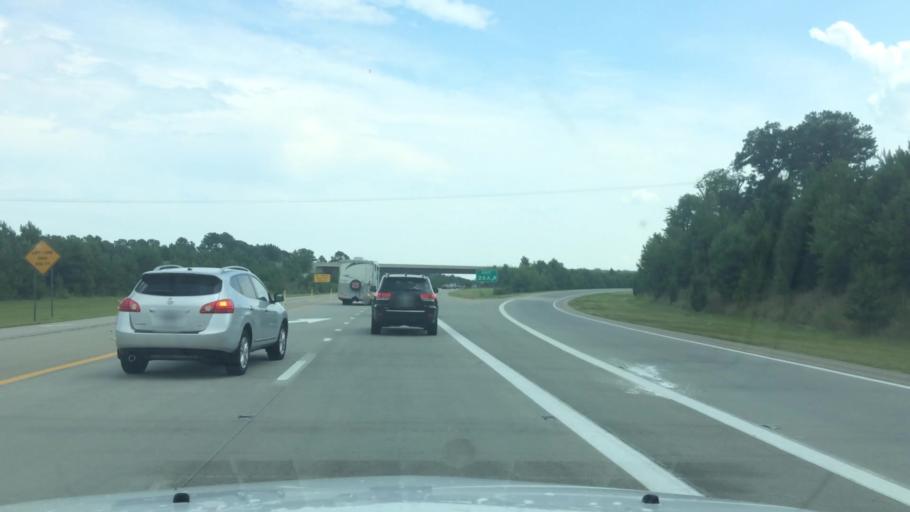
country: US
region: North Carolina
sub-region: Wake County
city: Knightdale
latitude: 35.7722
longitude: -78.5070
